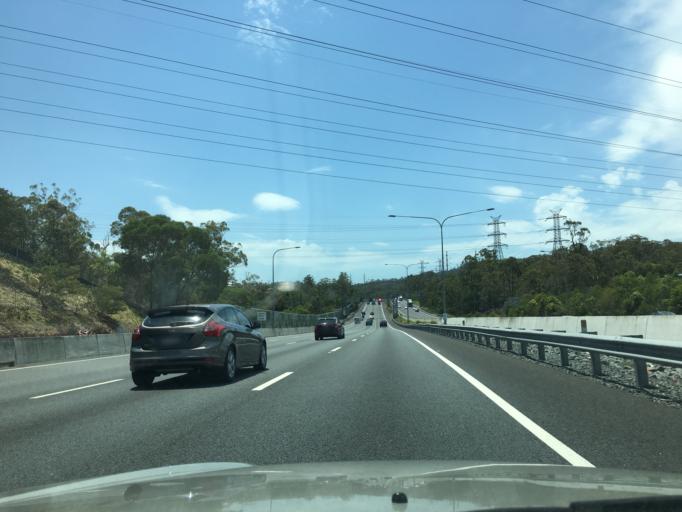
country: AU
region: Queensland
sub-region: Brisbane
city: Mackenzie
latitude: -27.5386
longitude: 153.1185
